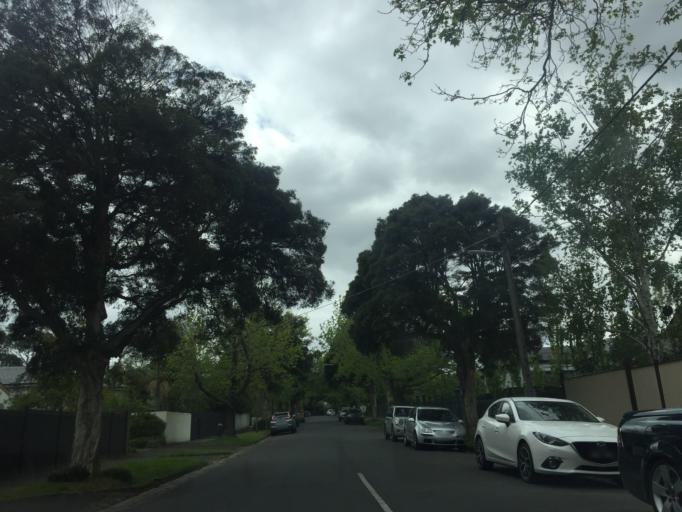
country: AU
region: Victoria
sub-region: Boroondara
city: Kew
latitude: -37.8079
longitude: 145.0425
